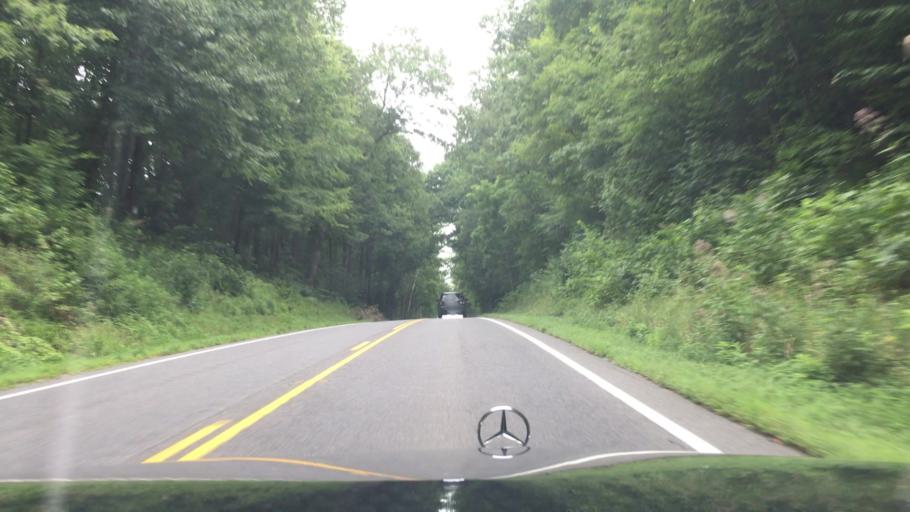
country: US
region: Virginia
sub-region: Nottoway County
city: Crewe
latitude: 37.2745
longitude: -78.1717
